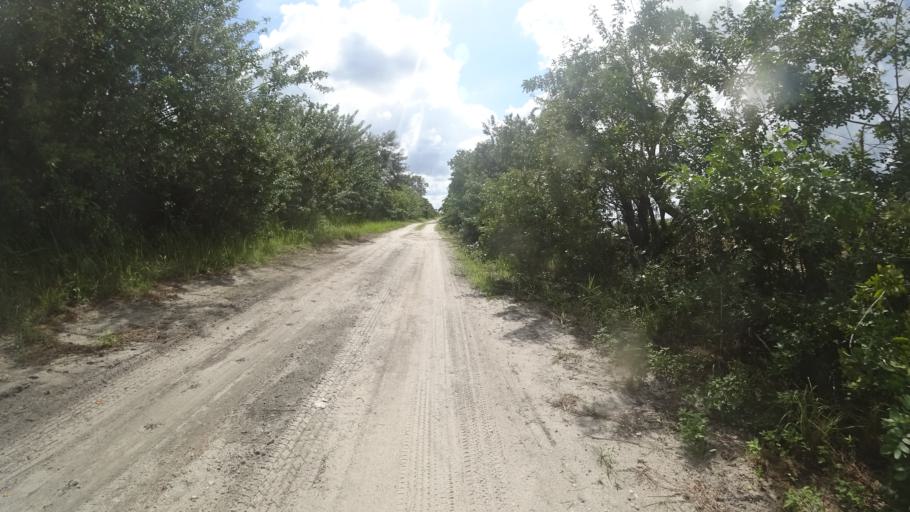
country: US
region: Florida
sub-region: Hillsborough County
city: Wimauma
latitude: 27.5893
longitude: -82.2664
